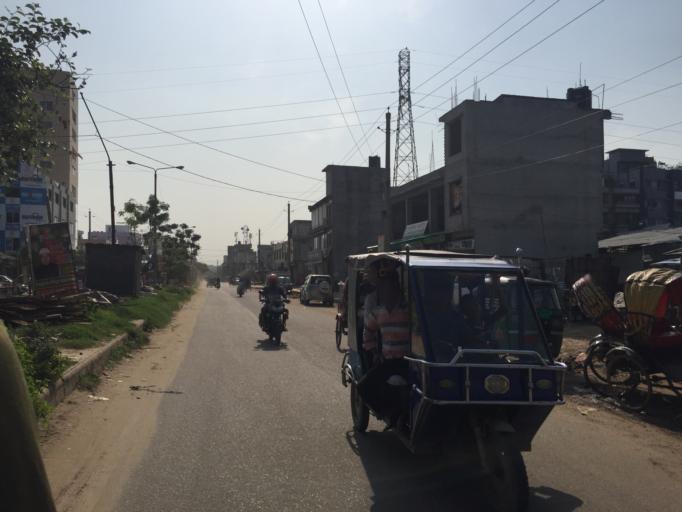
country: BD
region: Dhaka
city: Paltan
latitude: 23.7991
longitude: 90.4383
